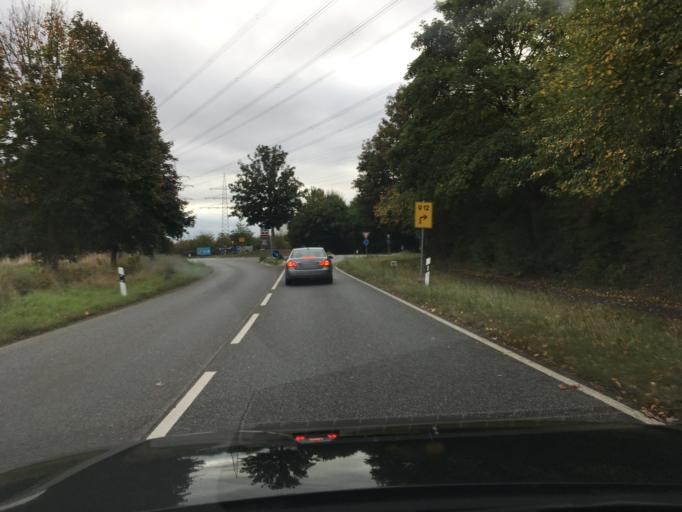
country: DE
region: Hesse
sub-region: Regierungsbezirk Giessen
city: Dehrn
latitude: 50.4004
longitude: 8.0812
